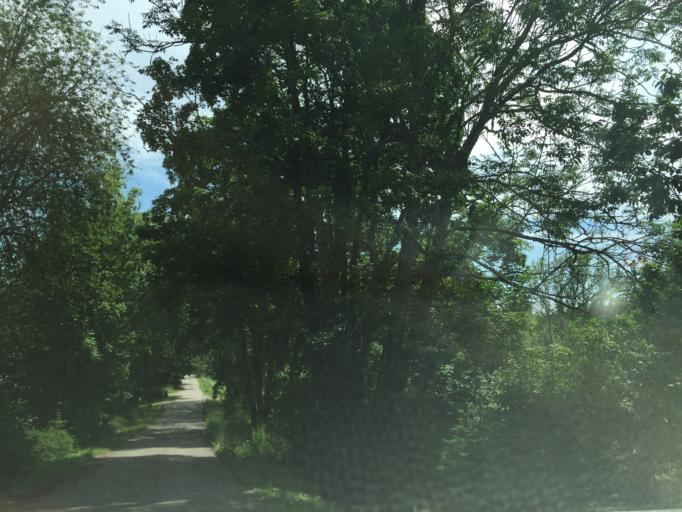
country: LV
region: Engure
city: Smarde
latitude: 57.0281
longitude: 23.2527
